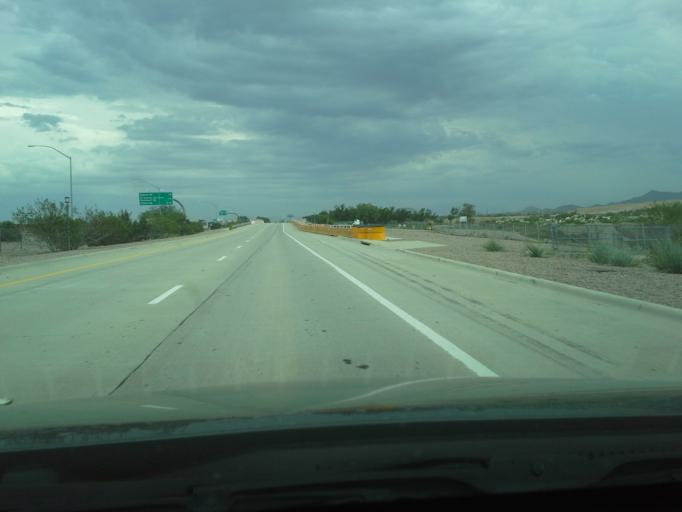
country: US
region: Arizona
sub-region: Pima County
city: Flowing Wells
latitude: 32.3170
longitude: -111.0479
